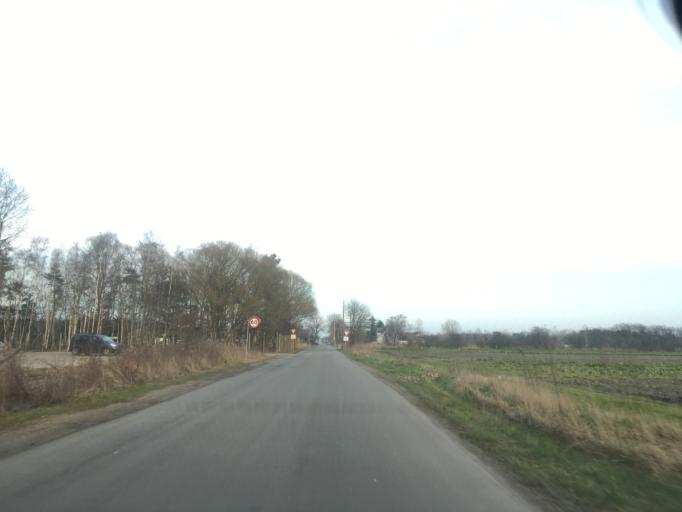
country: DK
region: Capital Region
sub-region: Tarnby Kommune
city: Tarnby
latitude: 55.5668
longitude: 12.5800
